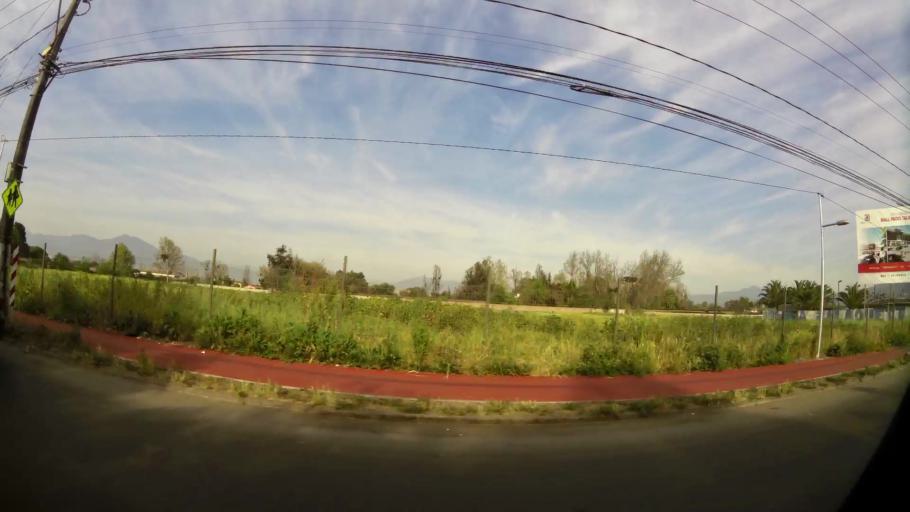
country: CL
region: Santiago Metropolitan
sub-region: Provincia de Talagante
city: Talagante
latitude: -33.6716
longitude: -70.9257
